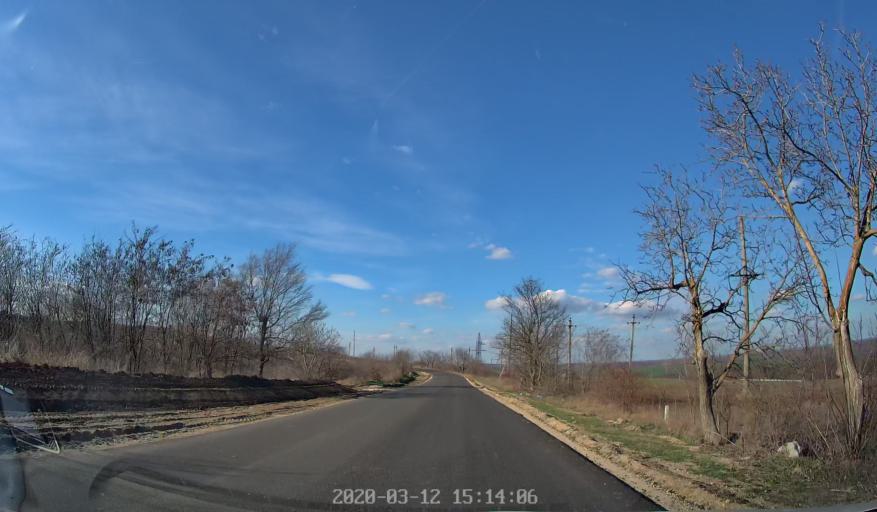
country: MD
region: Chisinau
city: Ciorescu
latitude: 47.2332
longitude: 28.9550
